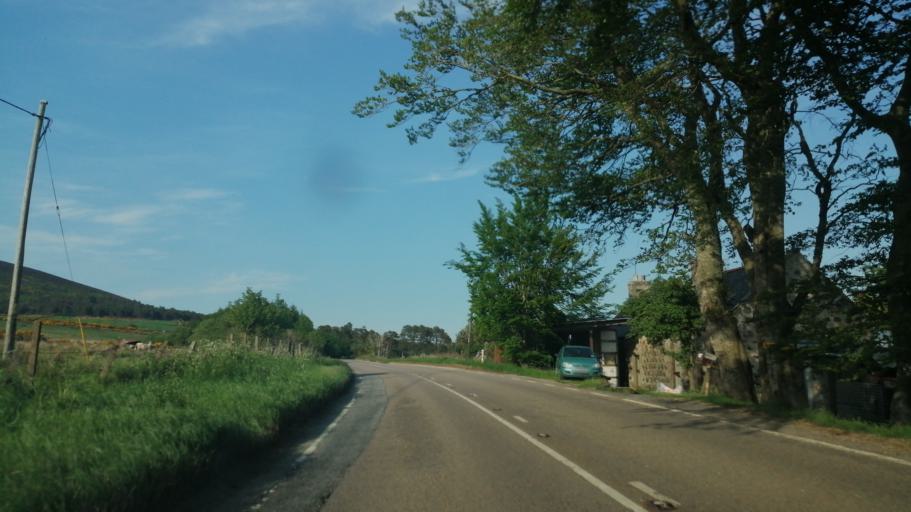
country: GB
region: Scotland
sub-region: Aberdeenshire
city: Huntly
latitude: 57.5677
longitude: -2.7847
